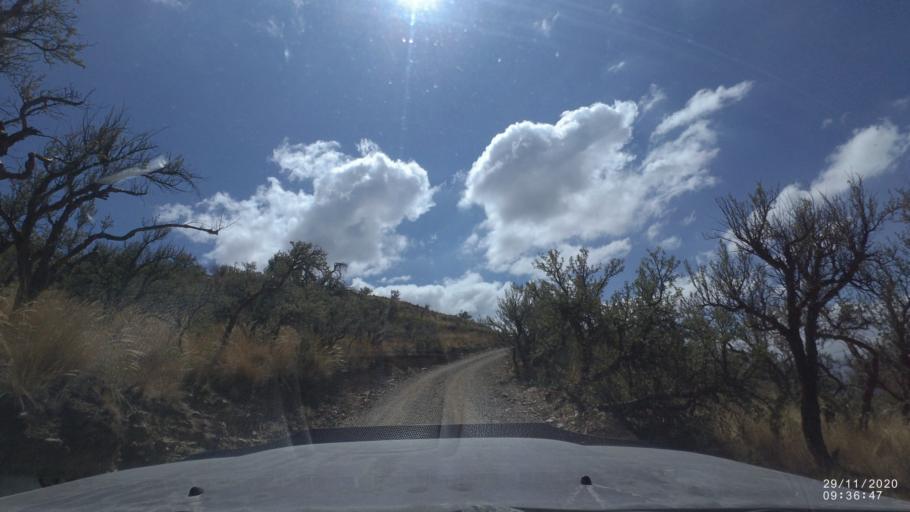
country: BO
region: Cochabamba
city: Cochabamba
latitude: -17.3091
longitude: -66.1873
